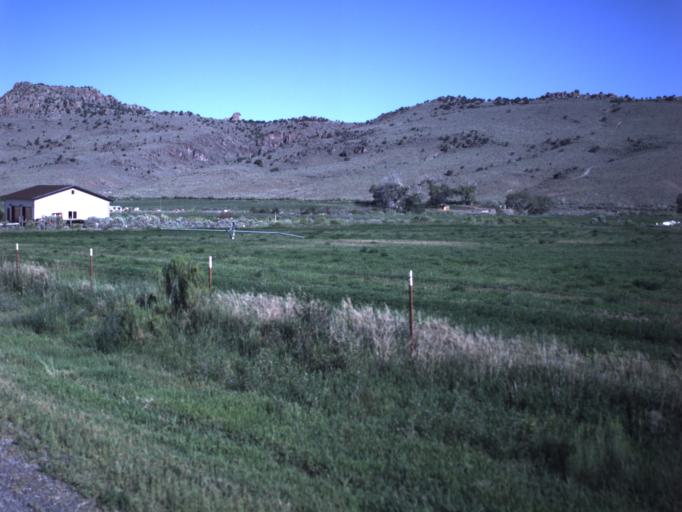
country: US
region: Utah
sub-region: Wayne County
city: Loa
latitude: 38.4694
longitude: -111.5893
